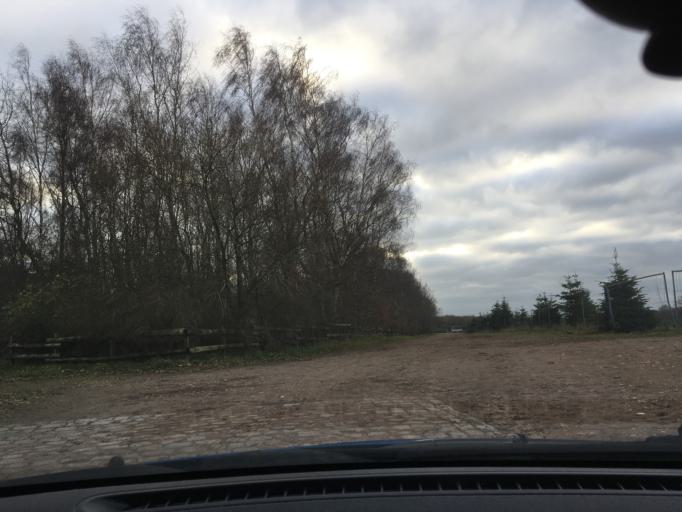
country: DE
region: Schleswig-Holstein
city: Poschendorf
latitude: 54.0324
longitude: 9.4726
